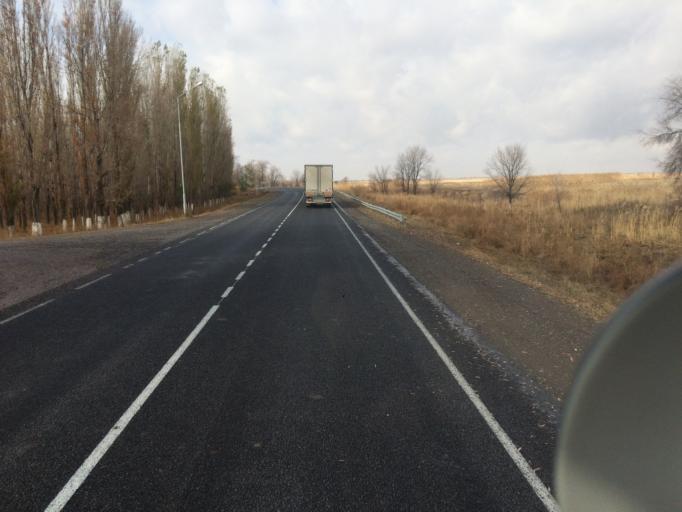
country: KZ
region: Zhambyl
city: Georgiyevka
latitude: 43.2222
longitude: 74.4504
